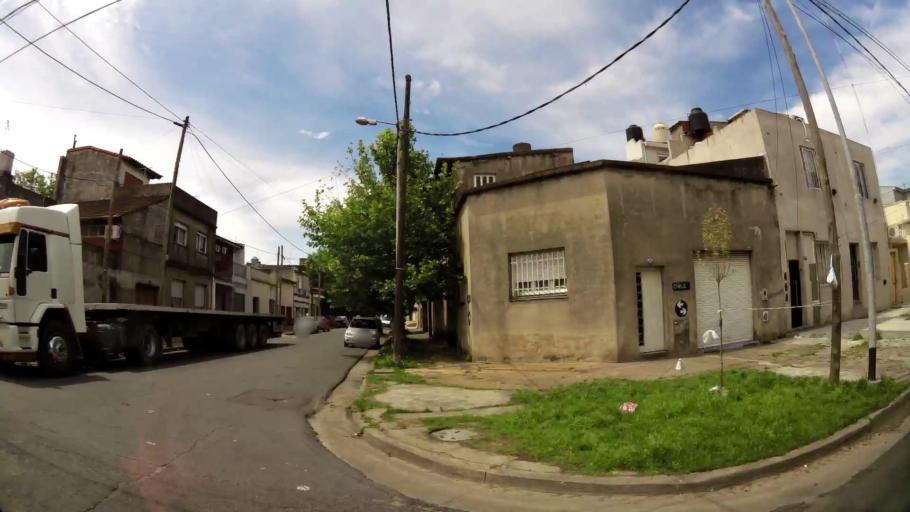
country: AR
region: Buenos Aires
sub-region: Partido de Avellaneda
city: Avellaneda
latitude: -34.6685
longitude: -58.4000
